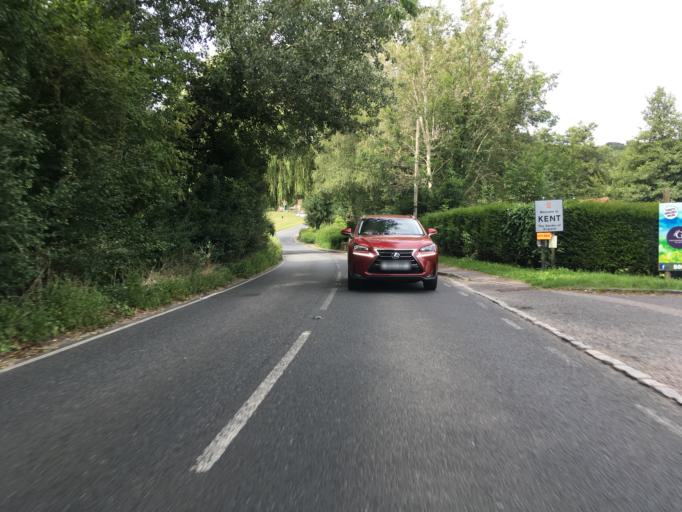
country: GB
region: England
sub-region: East Sussex
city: Crowborough
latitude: 51.1166
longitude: 0.1854
